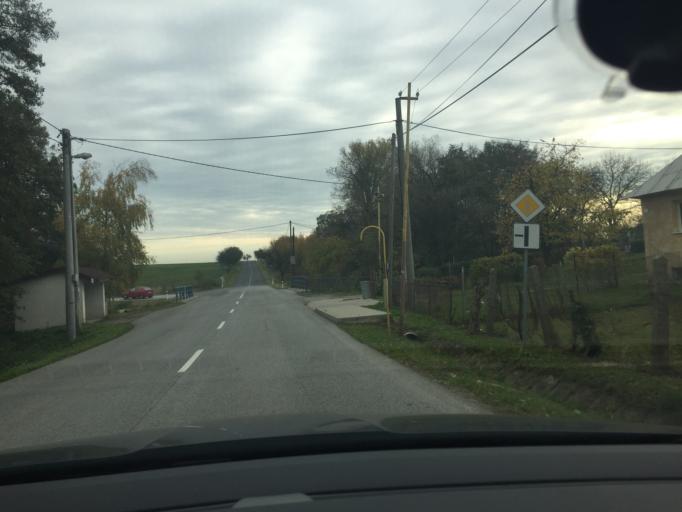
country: SK
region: Presovsky
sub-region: Okres Presov
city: Presov
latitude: 48.9162
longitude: 21.3237
